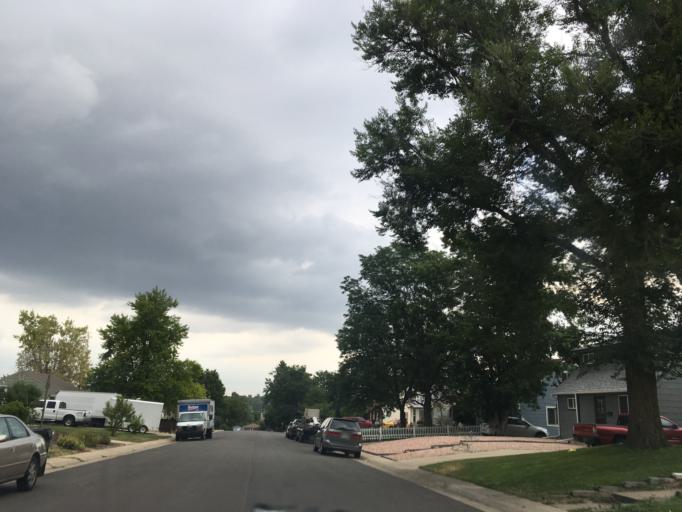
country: US
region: Colorado
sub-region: Arapahoe County
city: Englewood
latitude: 39.6868
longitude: -105.0070
